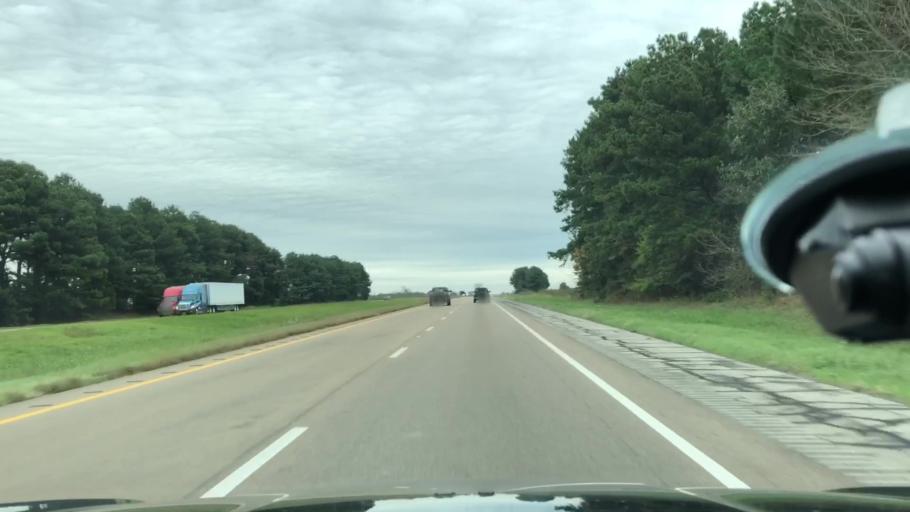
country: US
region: Texas
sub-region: Morris County
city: Omaha
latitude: 33.2835
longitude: -94.7925
